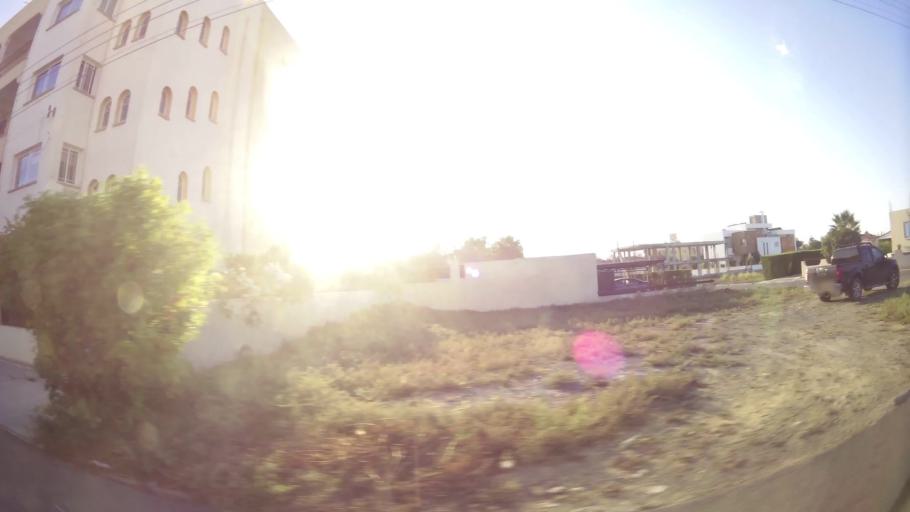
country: CY
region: Lefkosia
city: Nicosia
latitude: 35.2046
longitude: 33.3159
